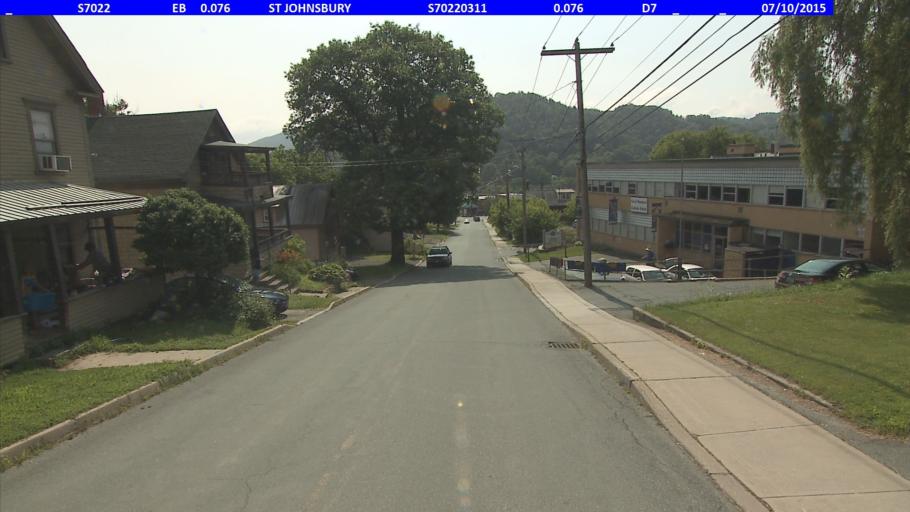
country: US
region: Vermont
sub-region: Caledonia County
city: Saint Johnsbury
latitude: 44.4208
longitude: -72.0180
